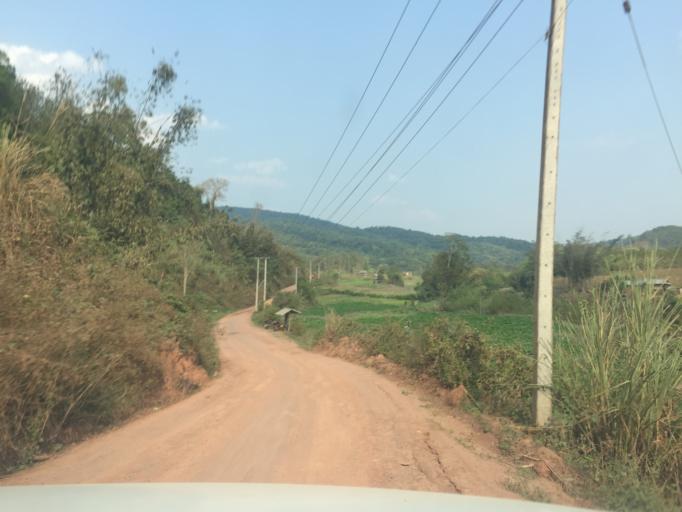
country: LA
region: Oudomxai
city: Muang La
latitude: 21.0741
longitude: 101.8243
